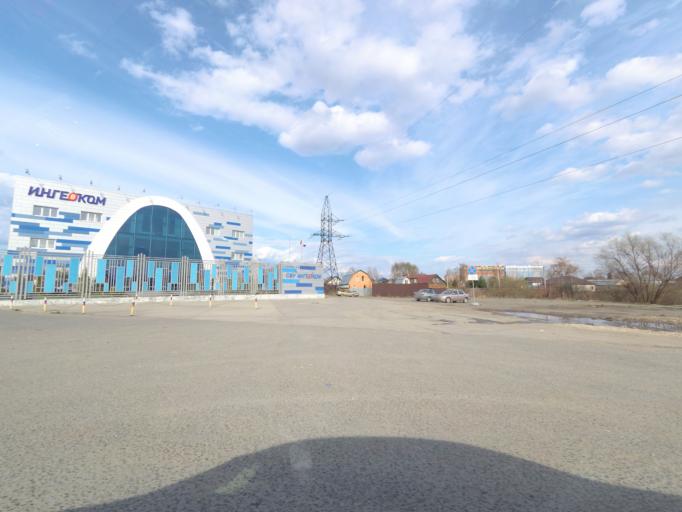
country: RU
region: Moskovskaya
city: Lobnya
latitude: 56.0087
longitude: 37.4374
